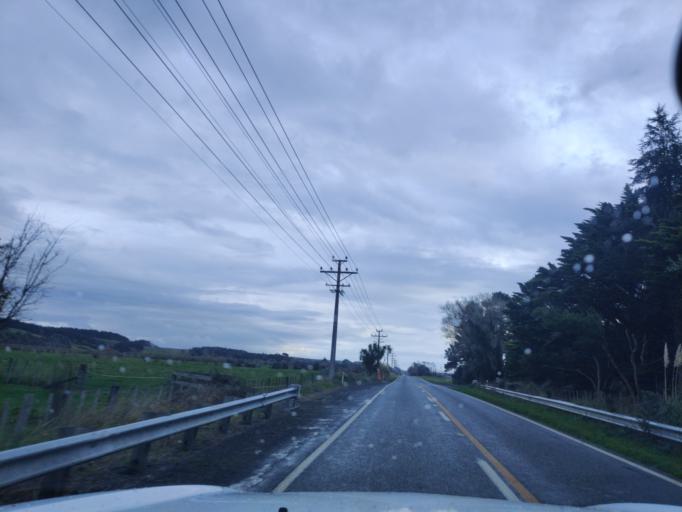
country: NZ
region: Manawatu-Wanganui
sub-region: Palmerston North City
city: Palmerston North
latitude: -40.3447
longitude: 175.7098
